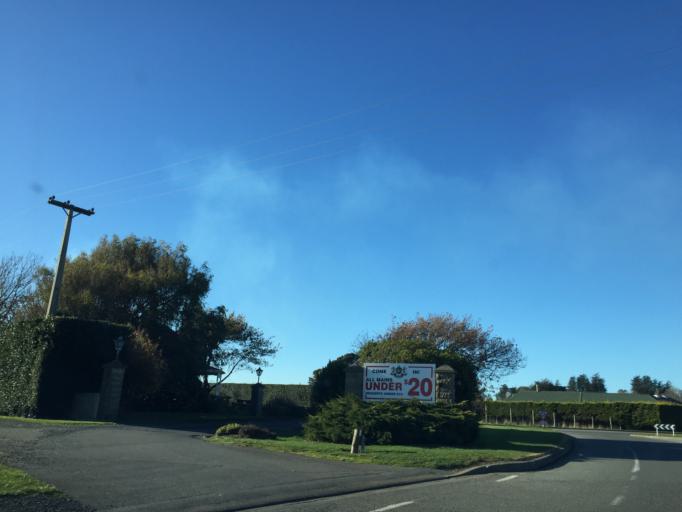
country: NZ
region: Southland
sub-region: Invercargill City
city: Invercargill
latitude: -46.3755
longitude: 168.3608
